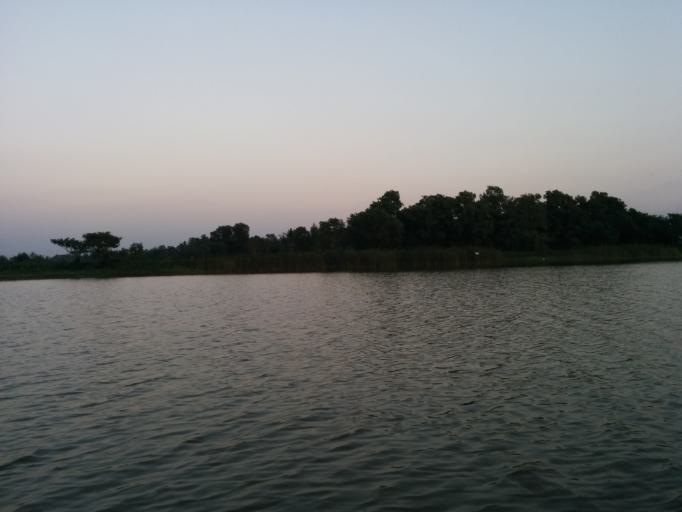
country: IN
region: Tamil Nadu
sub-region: Villupuram
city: Auroville
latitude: 11.9568
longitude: 79.7506
